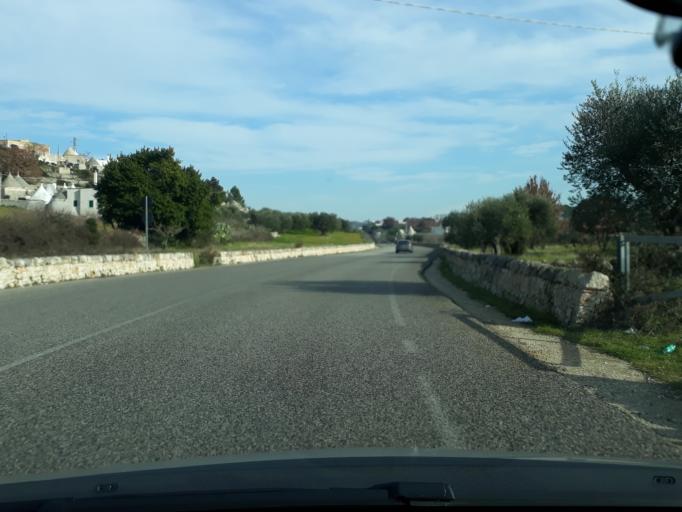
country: IT
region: Apulia
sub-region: Provincia di Bari
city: Locorotondo
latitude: 40.7510
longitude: 17.3399
